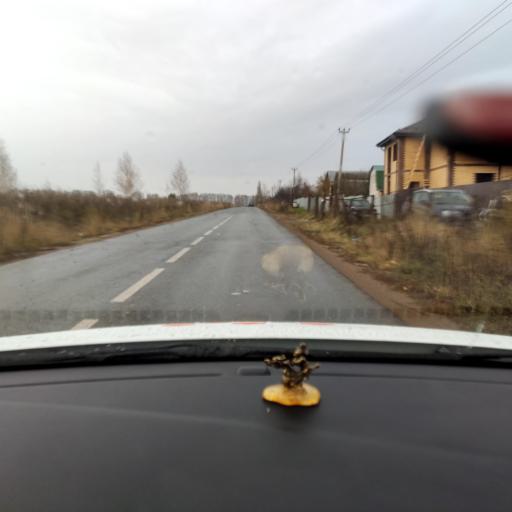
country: RU
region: Tatarstan
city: Vysokaya Gora
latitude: 55.8299
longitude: 49.2296
